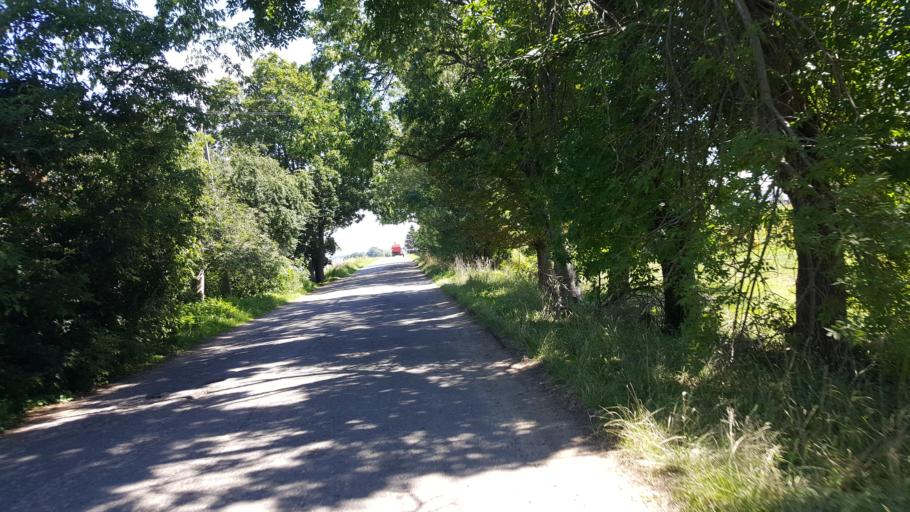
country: BY
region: Brest
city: Charnawchytsy
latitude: 52.2198
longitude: 23.7429
